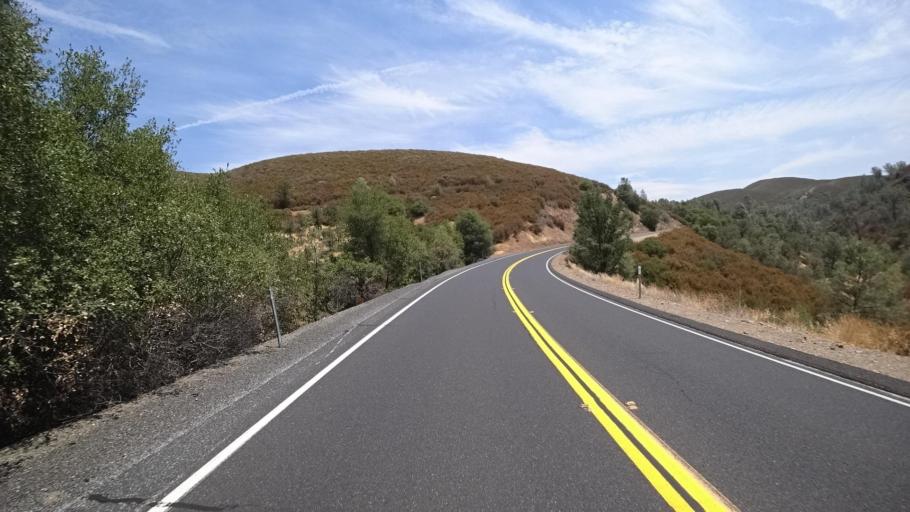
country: US
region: California
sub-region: Tuolumne County
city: Tuolumne City
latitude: 37.7094
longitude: -120.2241
